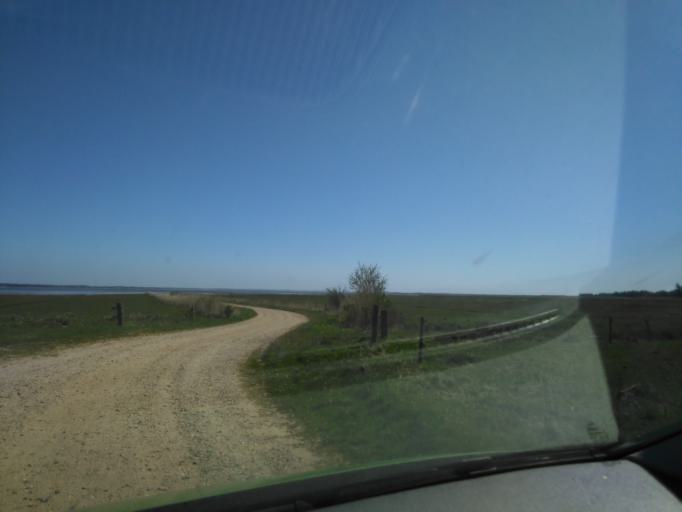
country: DK
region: South Denmark
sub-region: Varde Kommune
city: Oksbol
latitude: 55.5534
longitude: 8.2336
